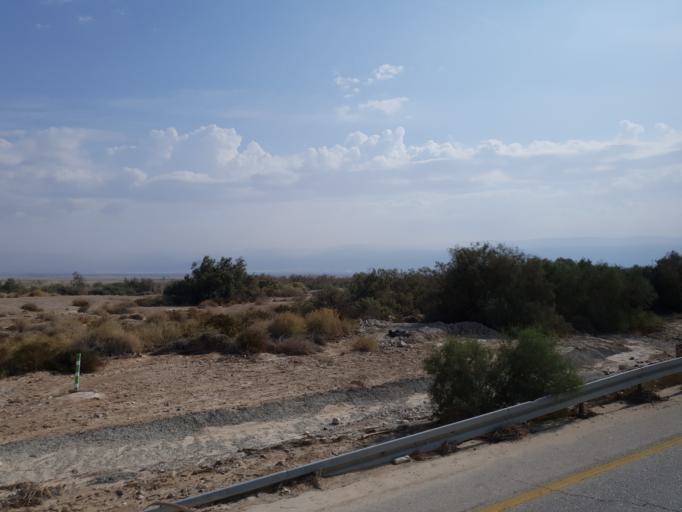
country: PS
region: West Bank
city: Jericho
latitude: 31.7845
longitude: 35.5007
